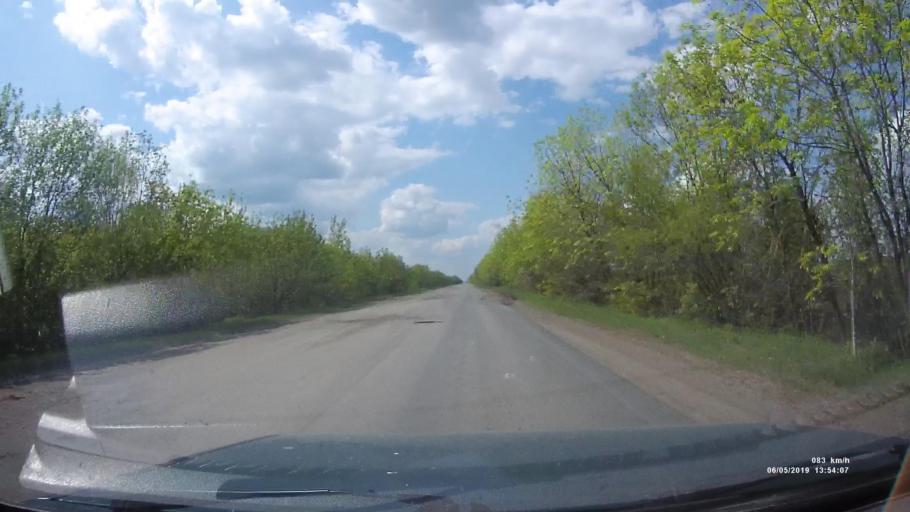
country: RU
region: Rostov
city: Melikhovskaya
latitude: 47.6726
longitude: 40.4518
